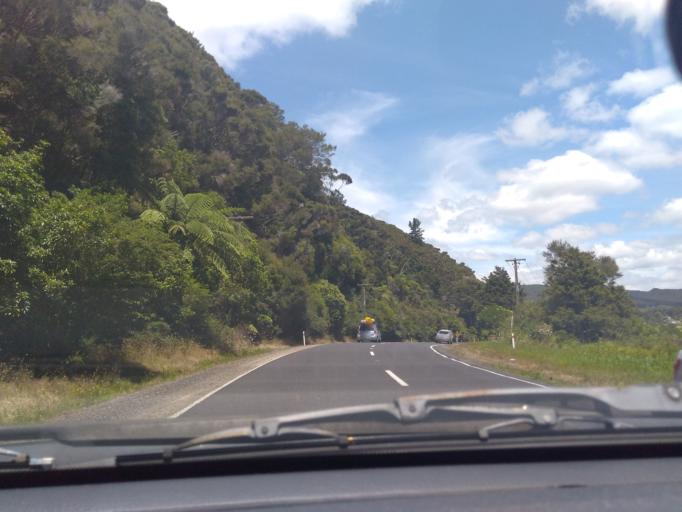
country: NZ
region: Northland
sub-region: Far North District
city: Kerikeri
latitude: -35.0890
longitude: 173.7671
